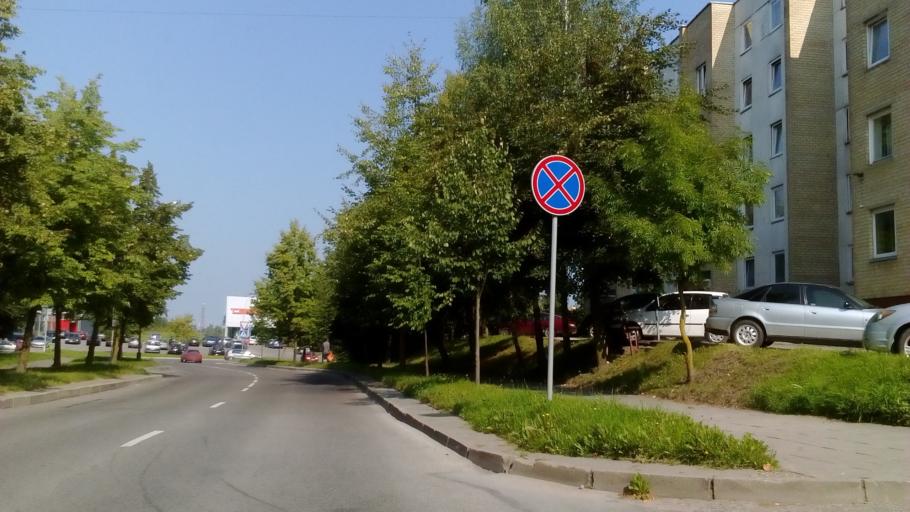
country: LT
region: Alytaus apskritis
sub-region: Alytus
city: Alytus
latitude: 54.3990
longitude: 24.0190
